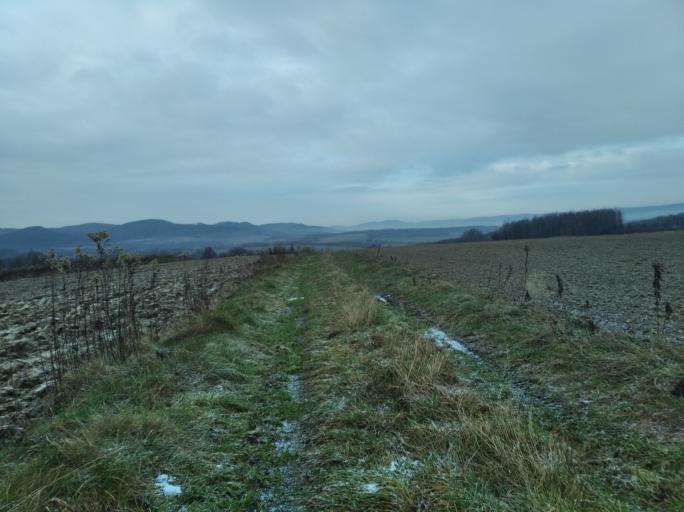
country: PL
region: Subcarpathian Voivodeship
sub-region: Powiat strzyzowski
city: Wysoka Strzyzowska
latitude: 49.8322
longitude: 21.7567
